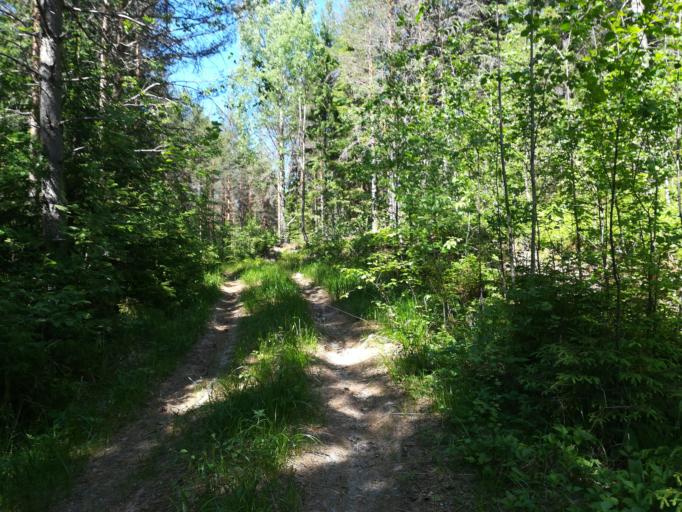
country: FI
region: Southern Savonia
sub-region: Mikkeli
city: Puumala
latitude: 61.6165
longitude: 28.1624
